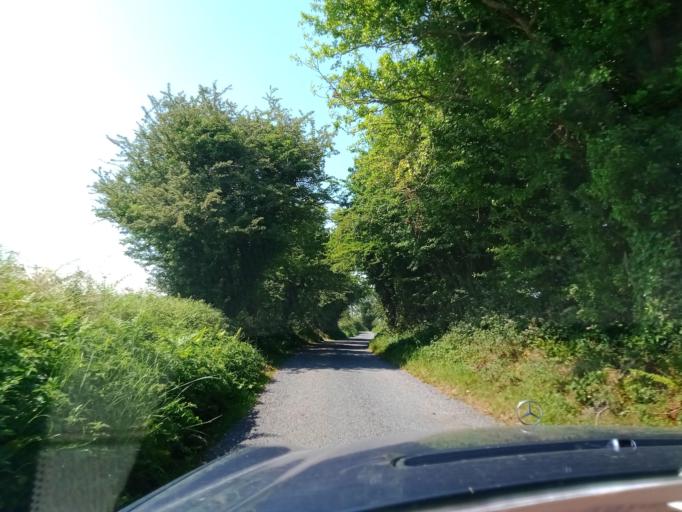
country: IE
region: Leinster
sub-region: Kilkenny
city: Mooncoin
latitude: 52.3188
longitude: -7.2833
